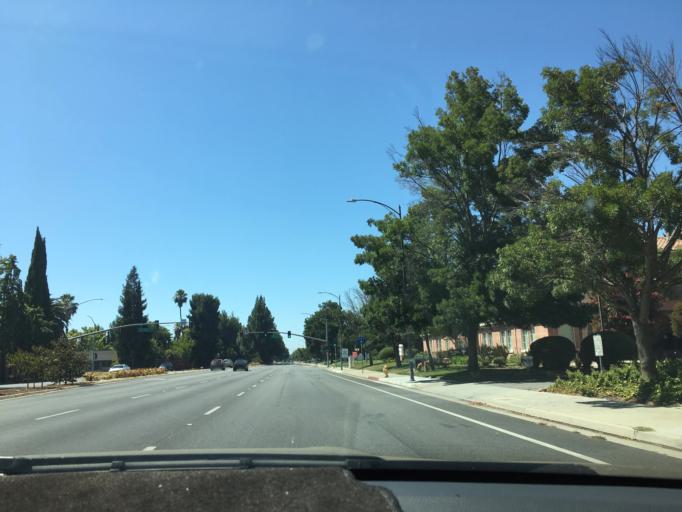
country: US
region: California
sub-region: Santa Clara County
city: Seven Trees
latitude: 37.2285
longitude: -121.7793
